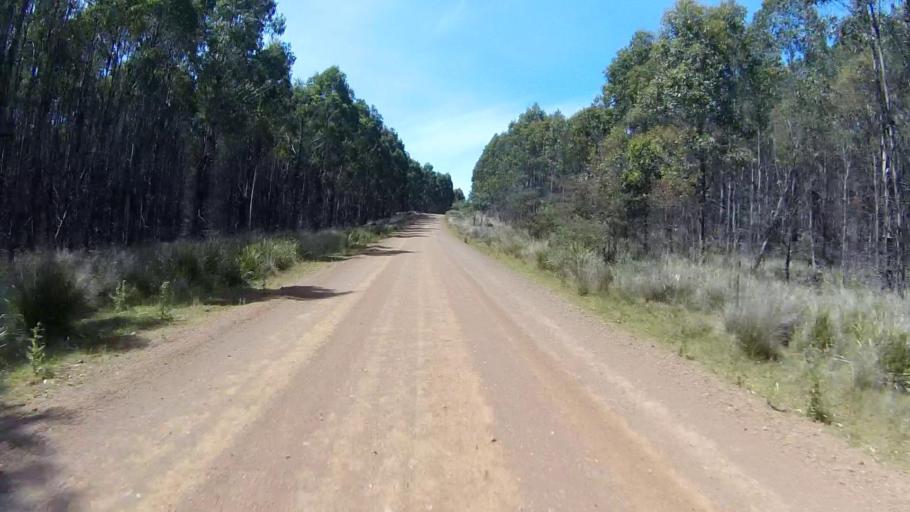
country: AU
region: Tasmania
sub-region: Sorell
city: Sorell
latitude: -42.6888
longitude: 147.7343
